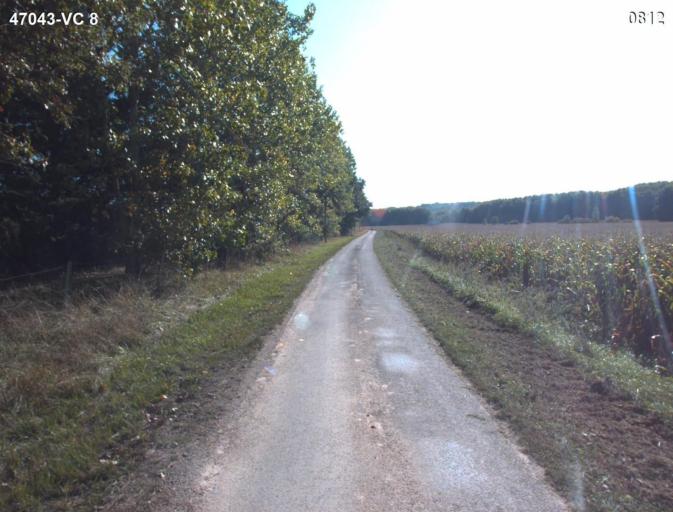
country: FR
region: Aquitaine
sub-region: Departement du Lot-et-Garonne
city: Buzet-sur-Baise
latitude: 44.2764
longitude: 0.2913
